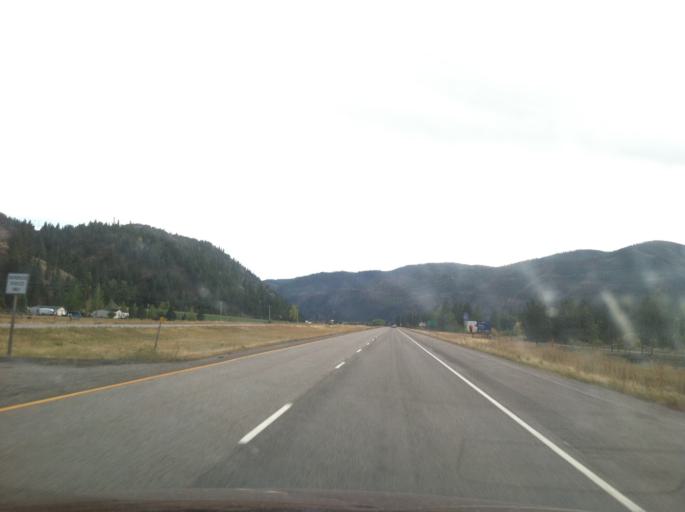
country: US
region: Montana
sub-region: Missoula County
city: Clinton
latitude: 46.7744
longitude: -113.7114
